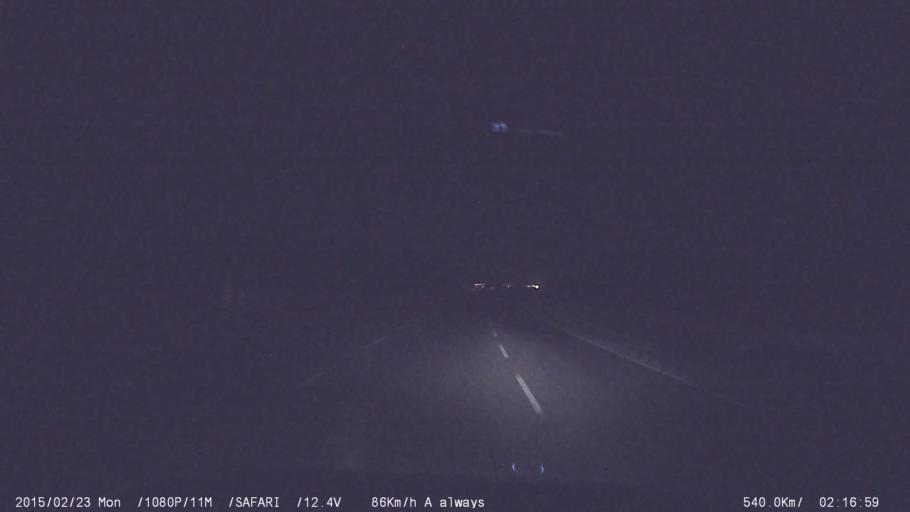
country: IN
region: Tamil Nadu
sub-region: Krishnagiri
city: Hosur
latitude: 12.7015
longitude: 77.9081
